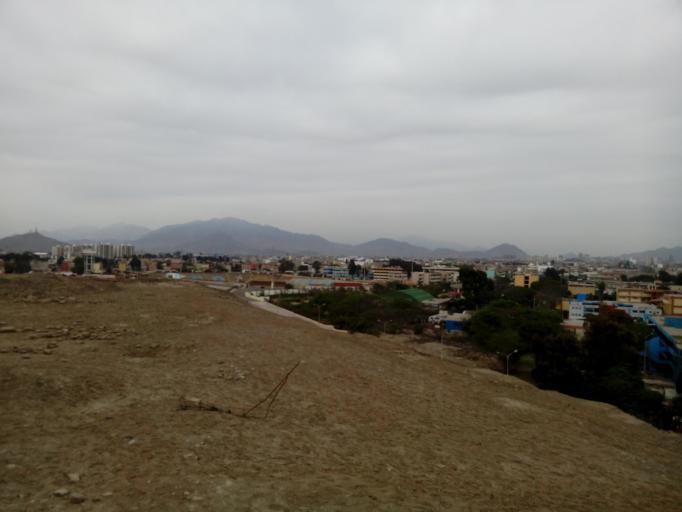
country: PE
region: Callao
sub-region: Callao
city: Callao
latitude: -12.0609
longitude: -77.0866
